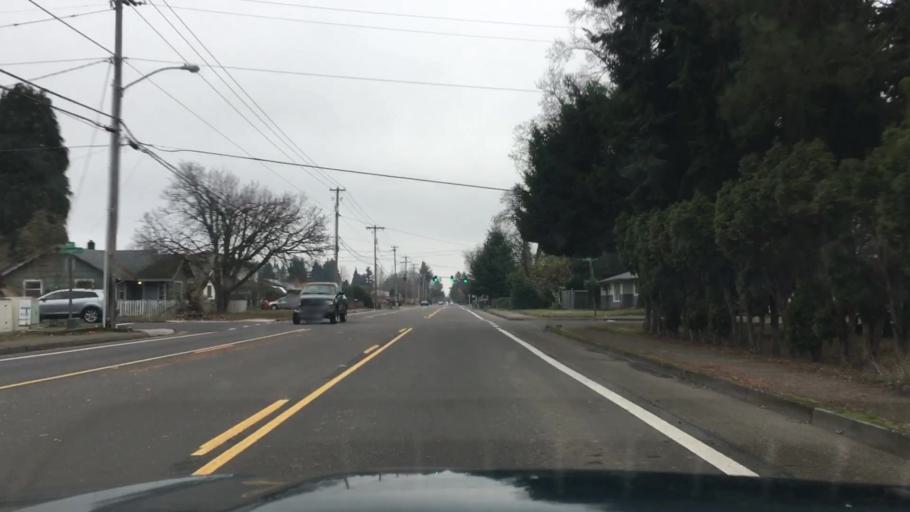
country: US
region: Oregon
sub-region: Lane County
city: Eugene
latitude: 44.0700
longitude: -123.1704
